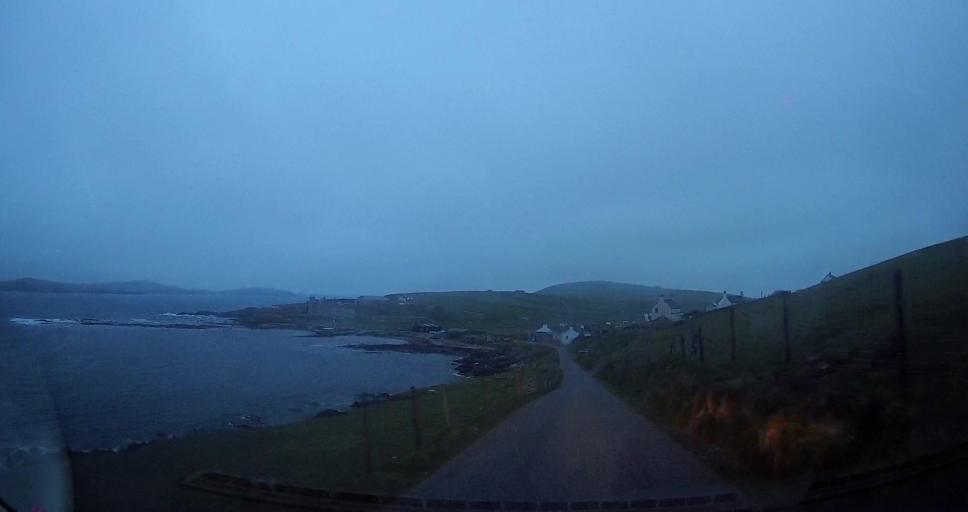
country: GB
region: Scotland
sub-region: Shetland Islands
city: Sandwick
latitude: 60.0089
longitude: -1.2251
